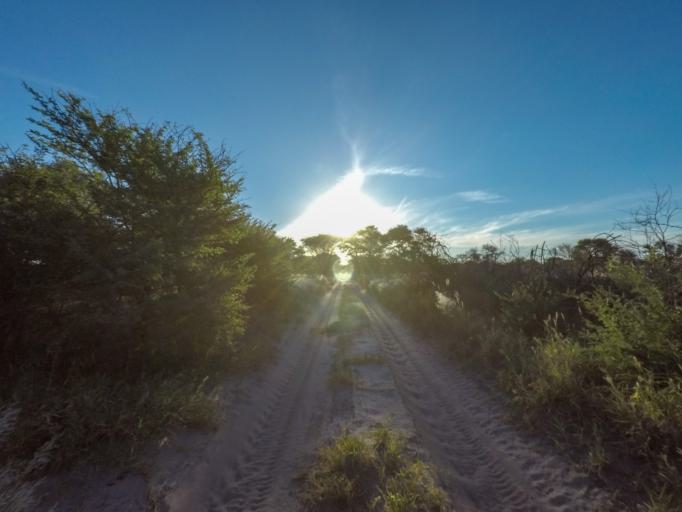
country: BW
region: Central
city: Rakops
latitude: -21.4049
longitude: 23.7815
